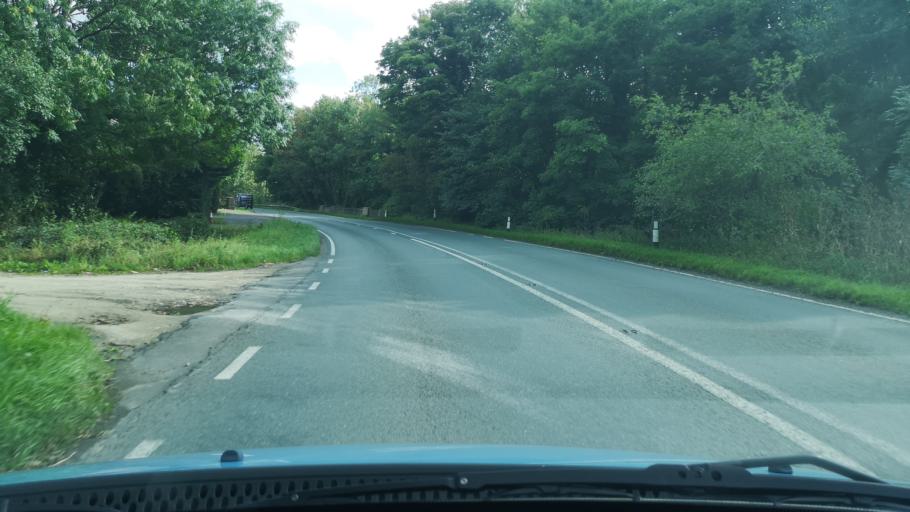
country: GB
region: England
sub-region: North Lincolnshire
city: Belton
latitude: 53.5795
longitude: -0.8212
